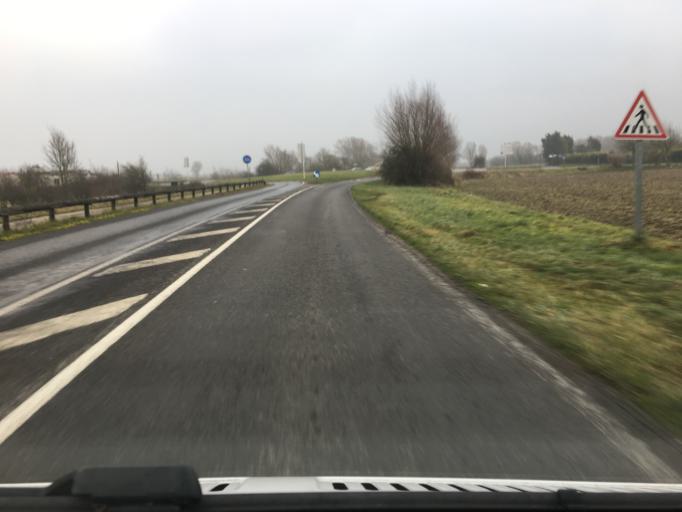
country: FR
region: Picardie
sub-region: Departement de la Somme
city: Le Crotoy
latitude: 50.2243
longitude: 1.6331
